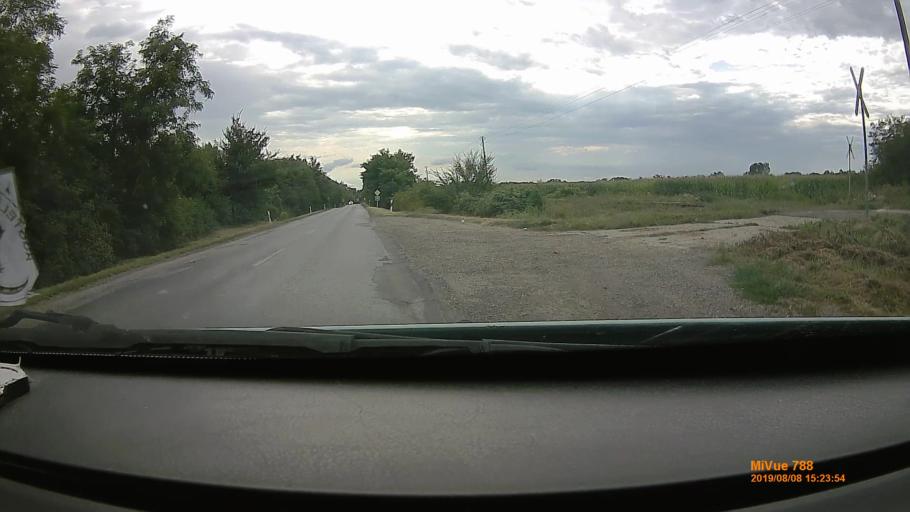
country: HU
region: Szabolcs-Szatmar-Bereg
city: Tunyogmatolcs
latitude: 47.9519
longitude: 22.4345
